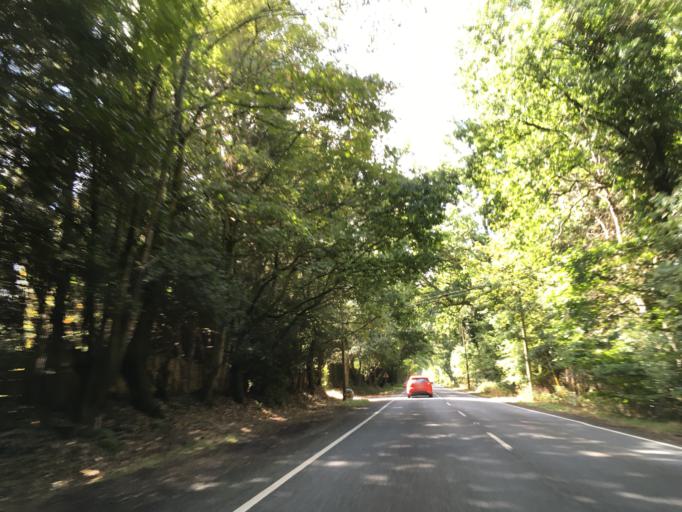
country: GB
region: England
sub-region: West Berkshire
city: Greenham
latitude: 51.3568
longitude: -1.3317
